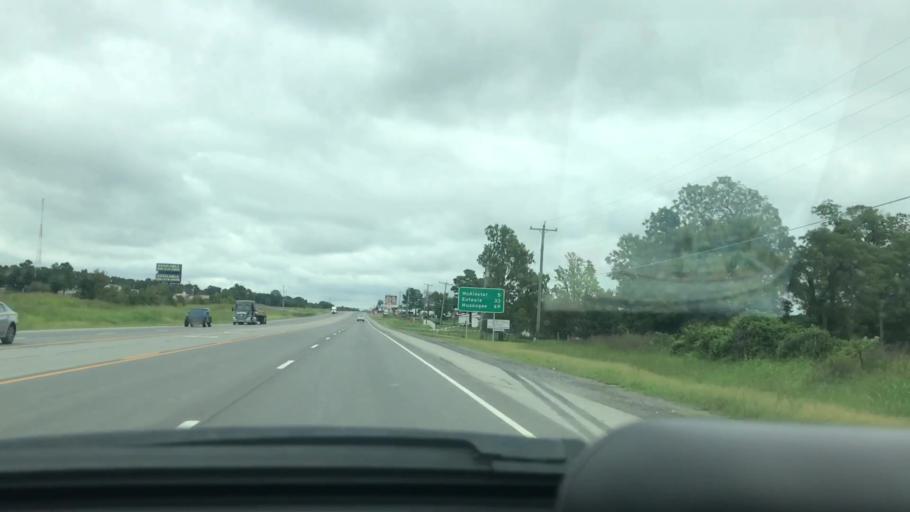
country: US
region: Oklahoma
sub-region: Pittsburg County
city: McAlester
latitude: 34.8697
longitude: -95.8056
